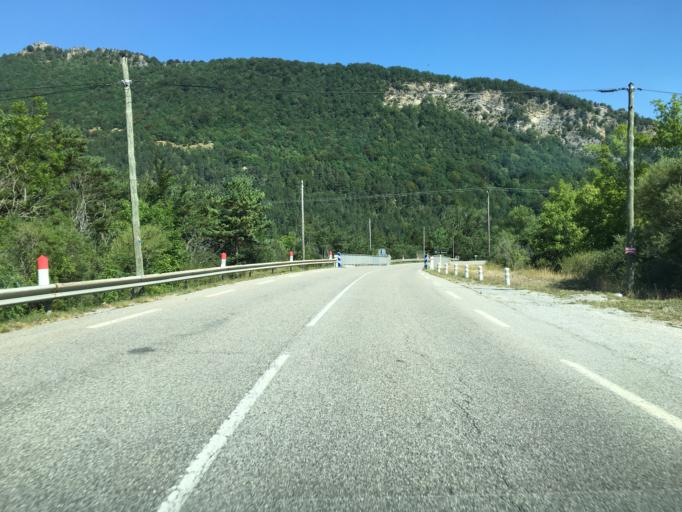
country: FR
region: Provence-Alpes-Cote d'Azur
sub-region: Departement des Hautes-Alpes
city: Veynes
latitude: 44.6382
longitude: 5.6957
